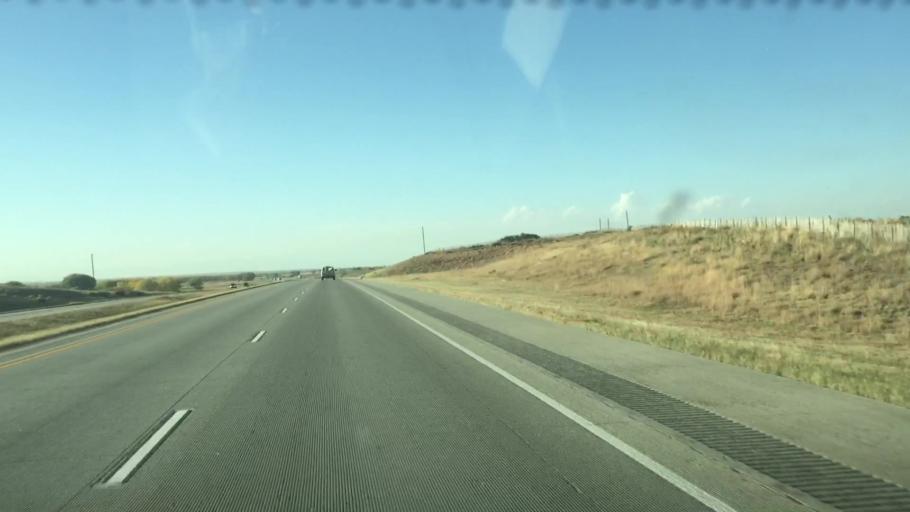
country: US
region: Colorado
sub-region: Lincoln County
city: Limon
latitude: 39.4856
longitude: -103.9535
